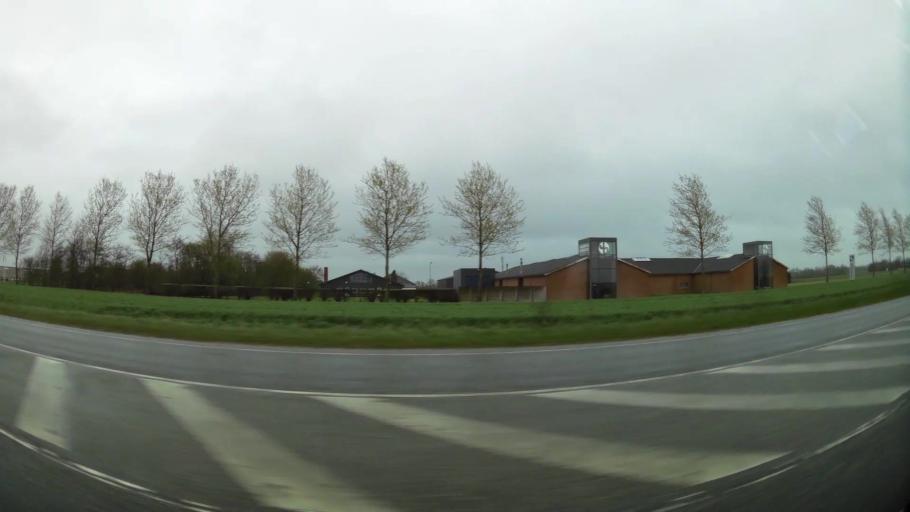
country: DK
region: Central Jutland
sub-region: Herning Kommune
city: Avlum
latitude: 56.2498
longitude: 8.7955
